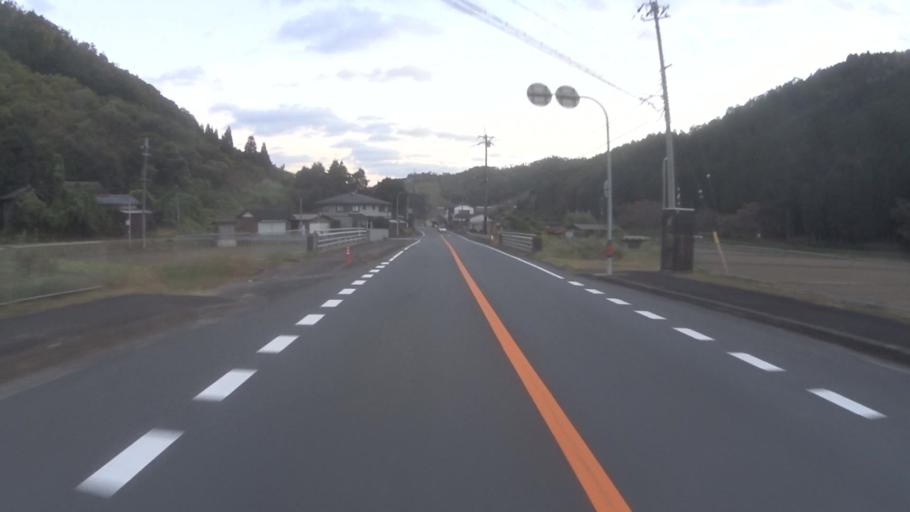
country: JP
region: Kyoto
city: Ayabe
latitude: 35.2107
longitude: 135.3505
